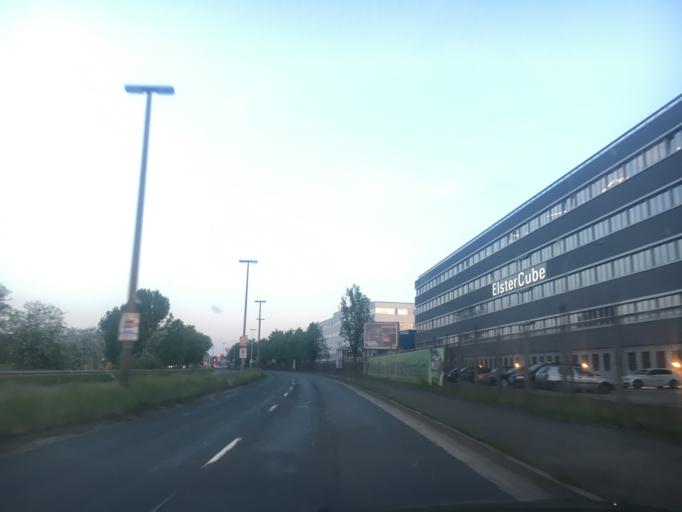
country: DE
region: Thuringia
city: Gera
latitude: 50.8580
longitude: 12.0761
